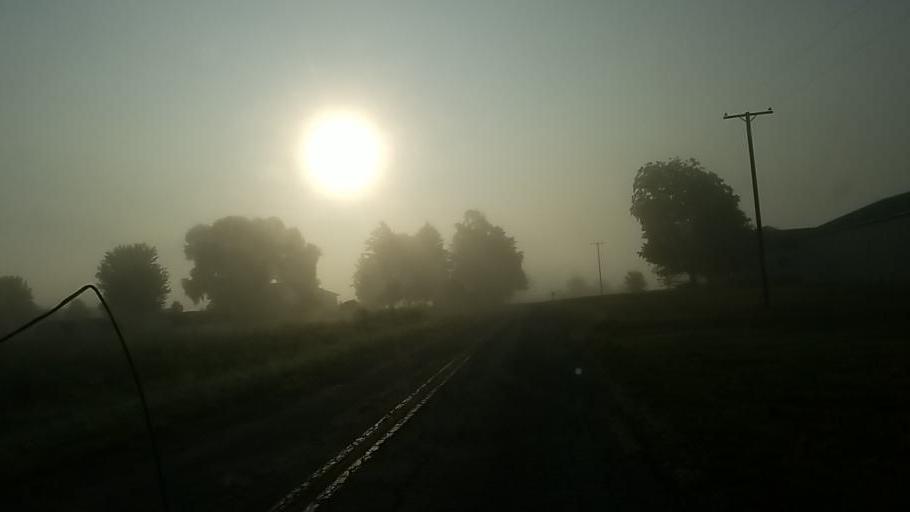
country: US
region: Michigan
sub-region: Newaygo County
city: Fremont
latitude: 43.4529
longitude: -86.0477
